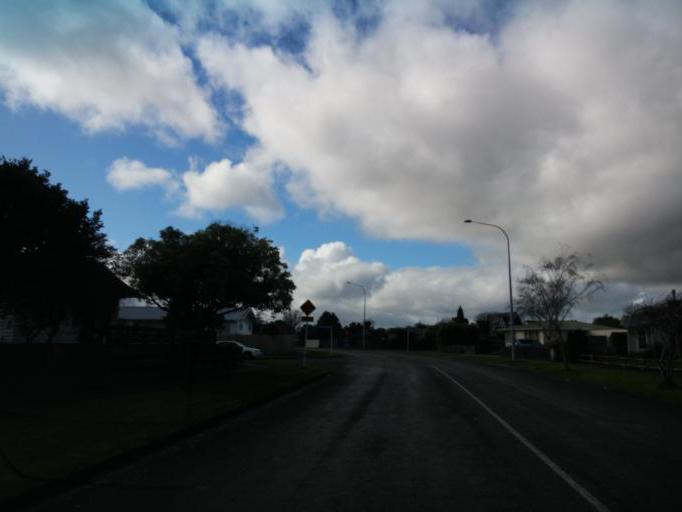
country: NZ
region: Manawatu-Wanganui
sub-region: Palmerston North City
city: Palmerston North
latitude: -40.3713
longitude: 175.5838
